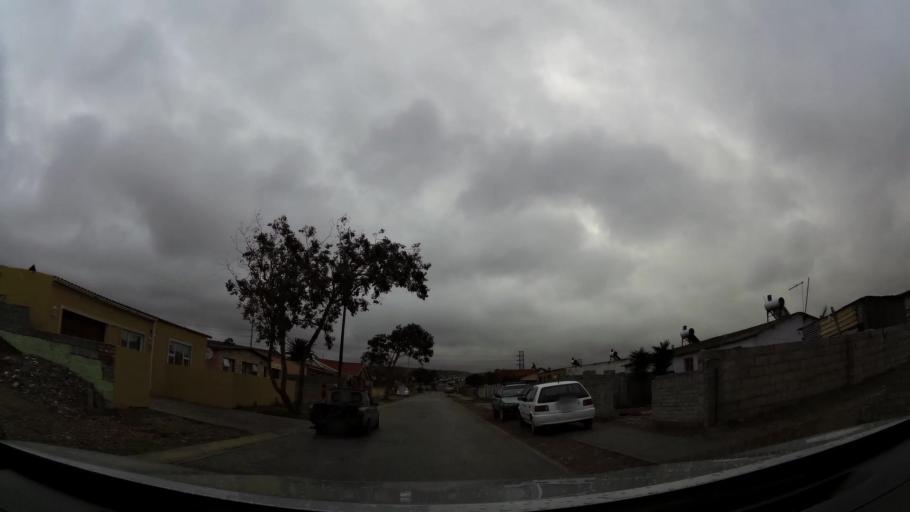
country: ZA
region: Eastern Cape
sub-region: Nelson Mandela Bay Metropolitan Municipality
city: Port Elizabeth
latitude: -33.8962
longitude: 25.5424
